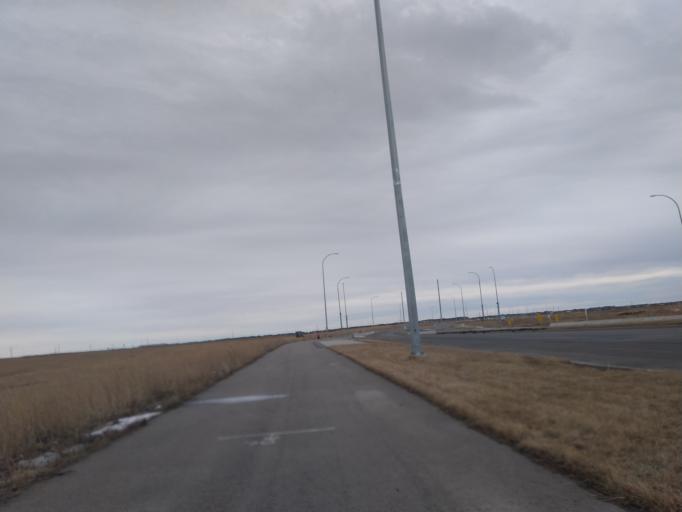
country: CA
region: Alberta
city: Airdrie
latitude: 51.1691
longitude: -113.9910
